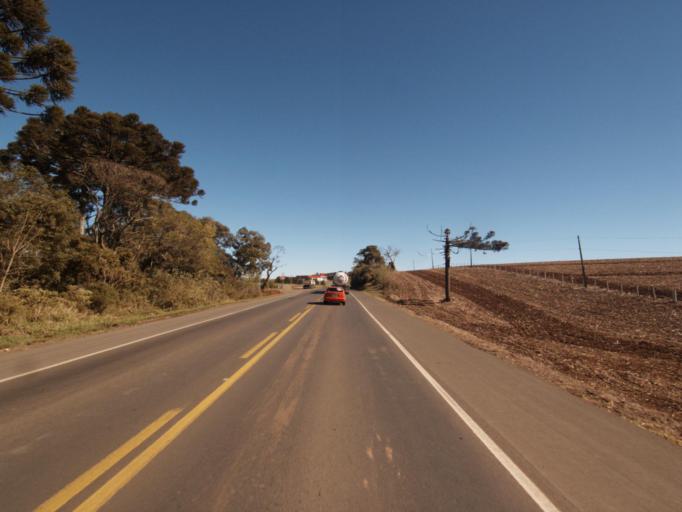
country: BR
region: Santa Catarina
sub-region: Xanxere
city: Xanxere
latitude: -26.8734
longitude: -52.2801
